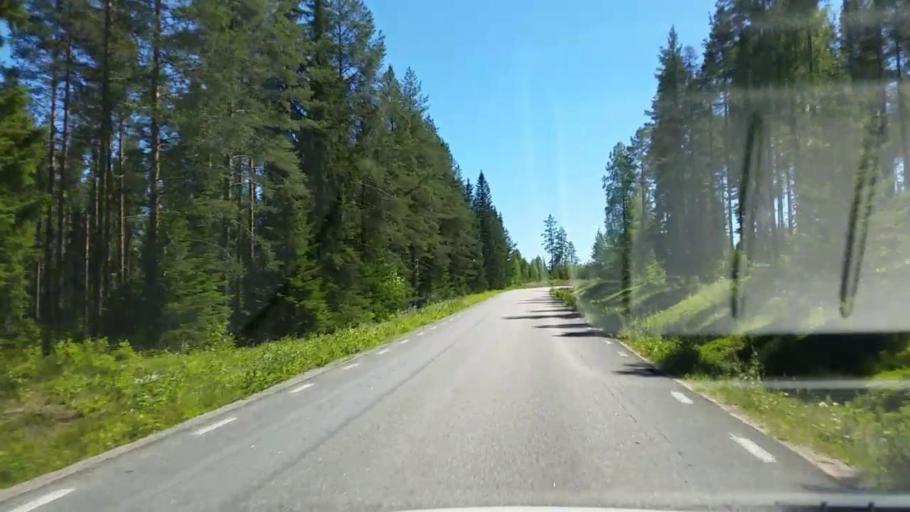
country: SE
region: Gaevleborg
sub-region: Ljusdals Kommun
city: Farila
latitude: 61.6475
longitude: 15.5911
